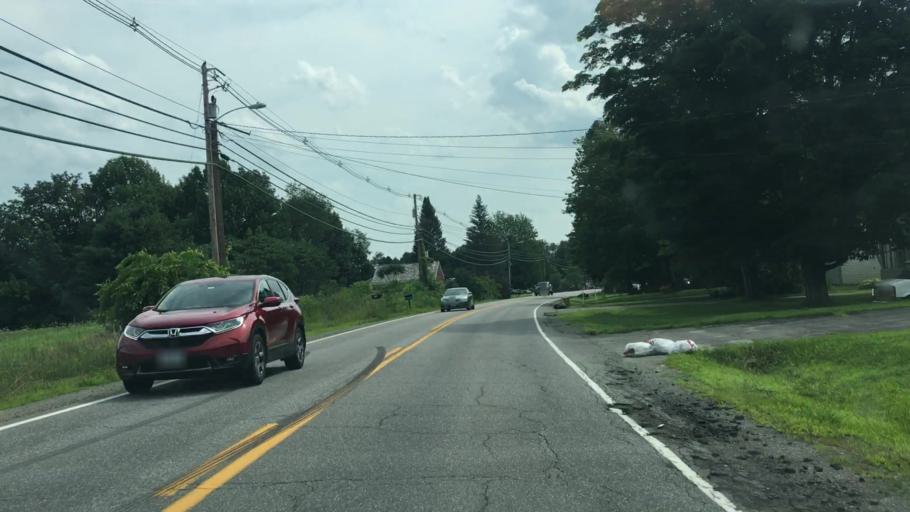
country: US
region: Maine
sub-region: Kennebec County
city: Winslow
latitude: 44.5097
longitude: -69.6308
